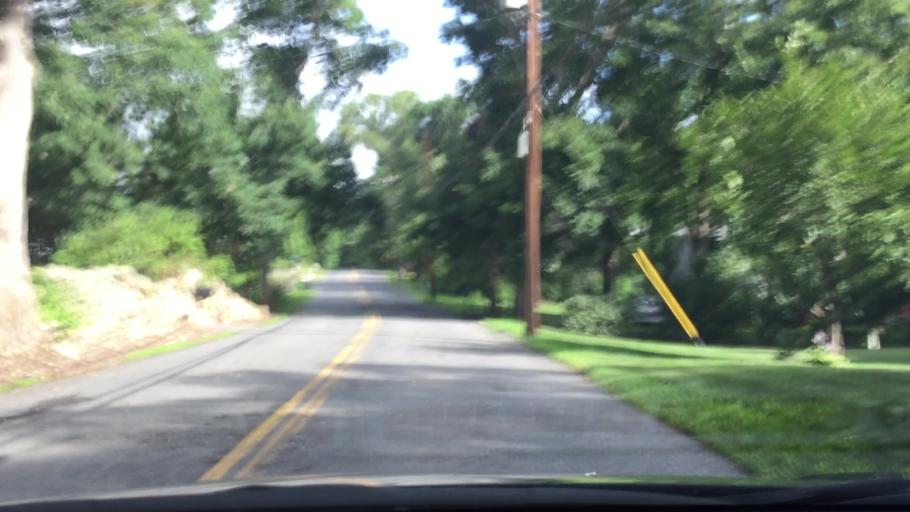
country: US
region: Massachusetts
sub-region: Middlesex County
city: Acton
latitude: 42.4896
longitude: -71.4325
